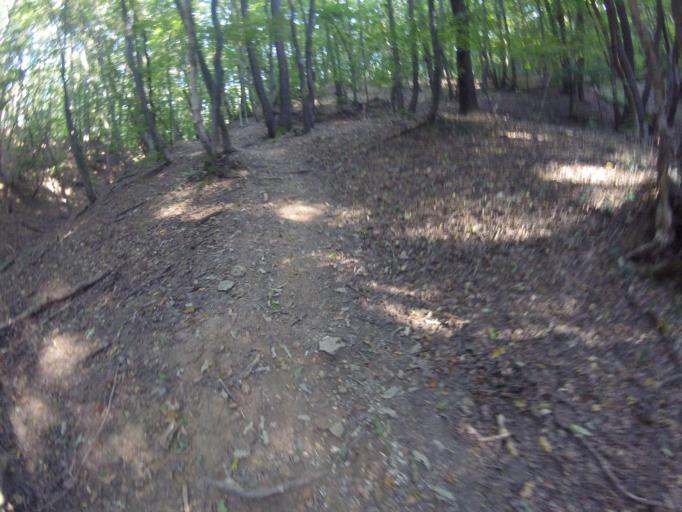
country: HU
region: Komarom-Esztergom
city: Piliscsev
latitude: 47.7084
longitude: 18.8381
